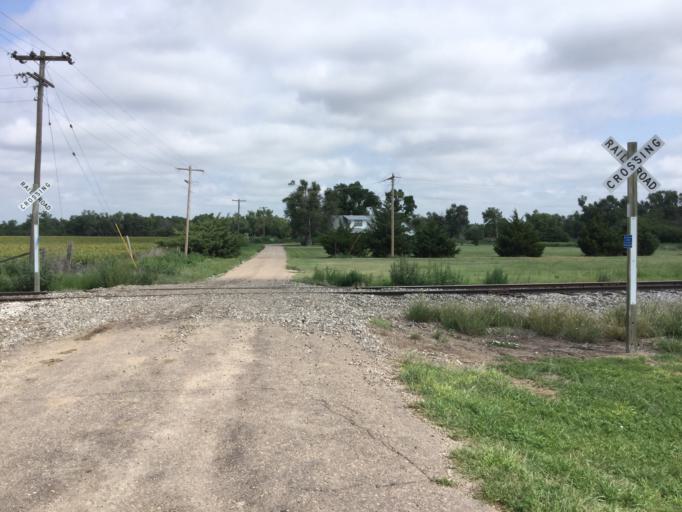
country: US
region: Kansas
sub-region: Rush County
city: La Crosse
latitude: 38.4669
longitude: -99.5577
